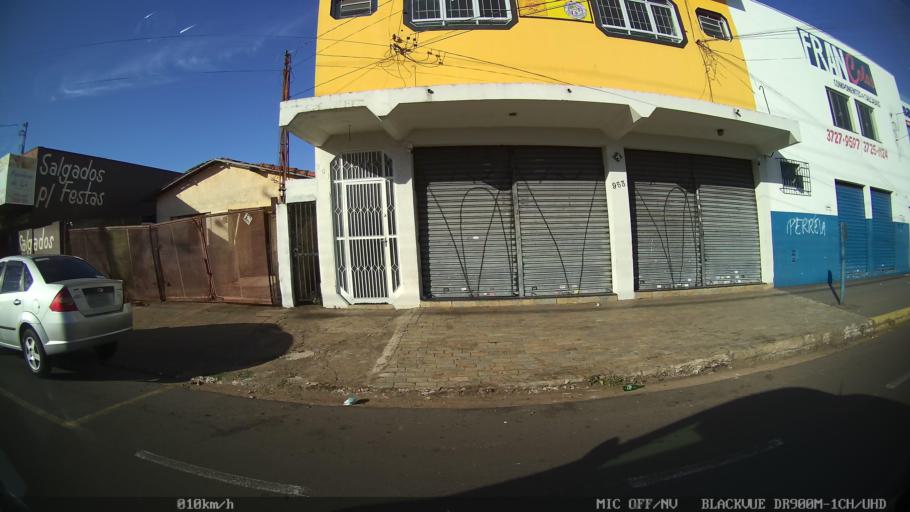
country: BR
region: Sao Paulo
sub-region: Franca
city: Franca
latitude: -20.5234
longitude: -47.3701
